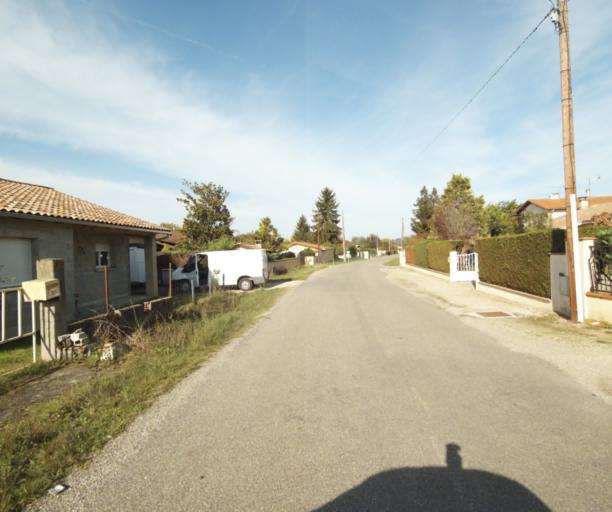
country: FR
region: Midi-Pyrenees
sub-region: Departement du Tarn-et-Garonne
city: Nohic
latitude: 43.9091
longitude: 1.4476
